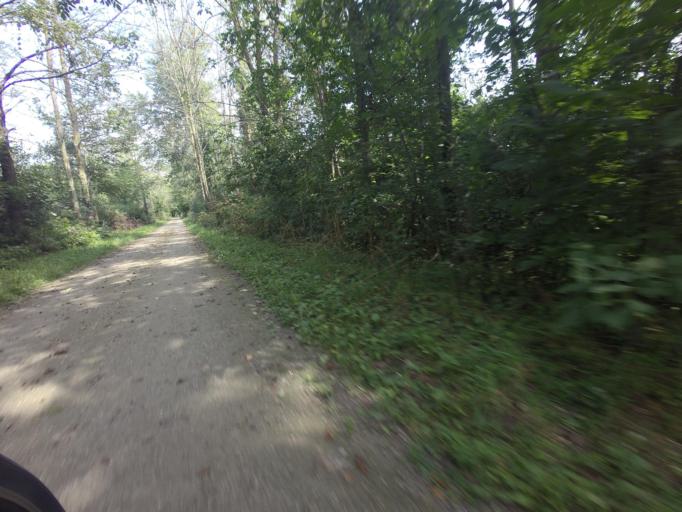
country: CA
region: Ontario
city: Waterloo
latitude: 43.5961
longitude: -80.6647
